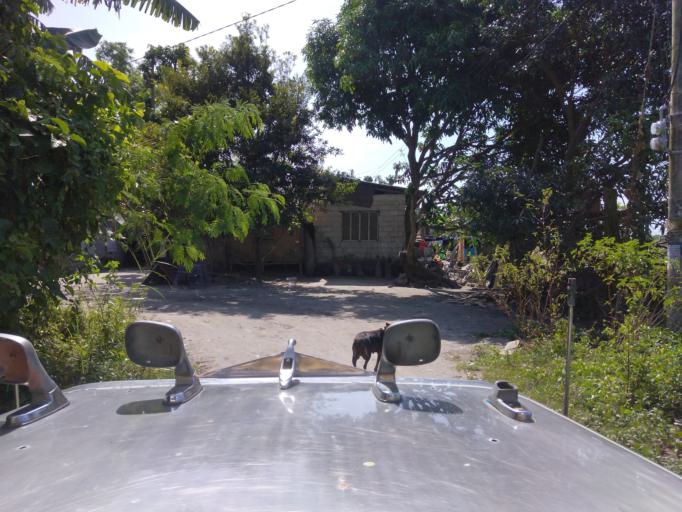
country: PH
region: Central Luzon
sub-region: Province of Pampanga
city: Bacolor
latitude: 15.0037
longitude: 120.6716
